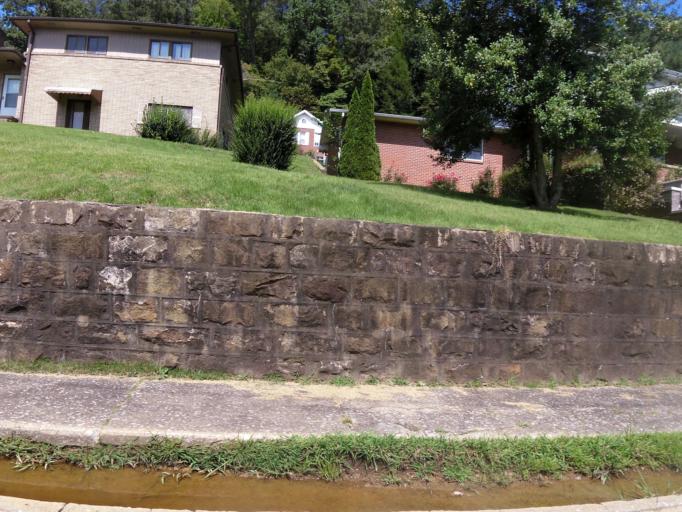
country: US
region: Kentucky
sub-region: Harlan County
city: Harlan
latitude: 36.8491
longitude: -83.3215
